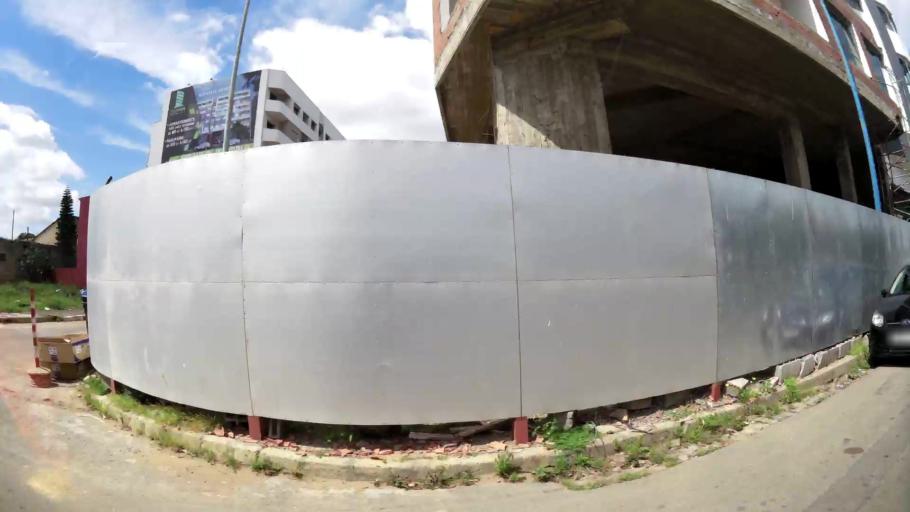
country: MA
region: Grand Casablanca
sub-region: Casablanca
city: Casablanca
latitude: 33.5592
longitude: -7.6256
